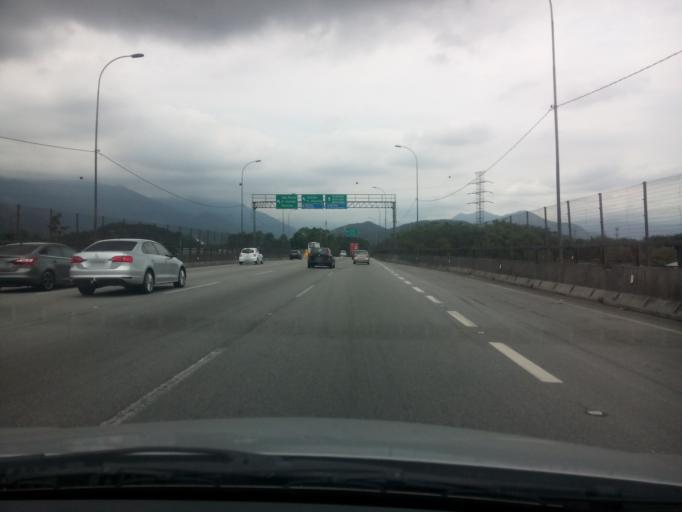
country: BR
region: Sao Paulo
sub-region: Cubatao
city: Cubatao
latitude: -23.8889
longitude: -46.4329
